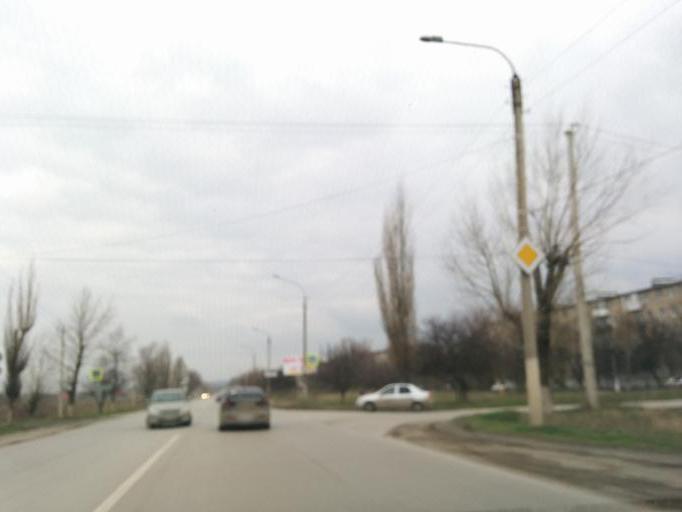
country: RU
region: Rostov
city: Krasyukovskaya
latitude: 47.4897
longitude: 40.1030
